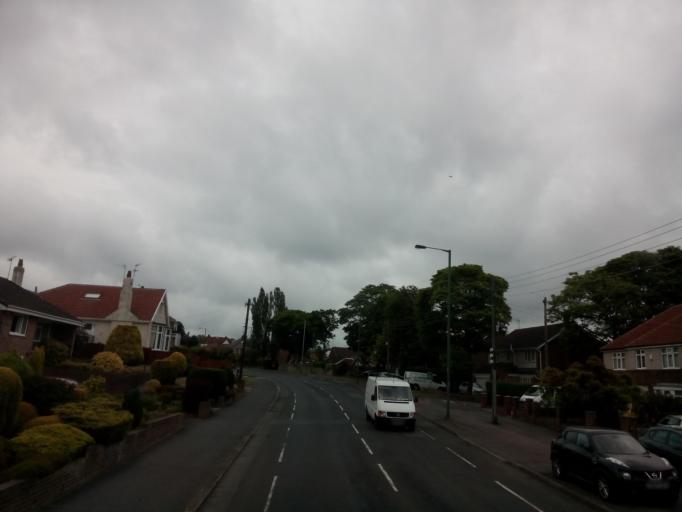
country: GB
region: England
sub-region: County Durham
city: Chester-le-Street
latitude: 54.8626
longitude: -1.5739
